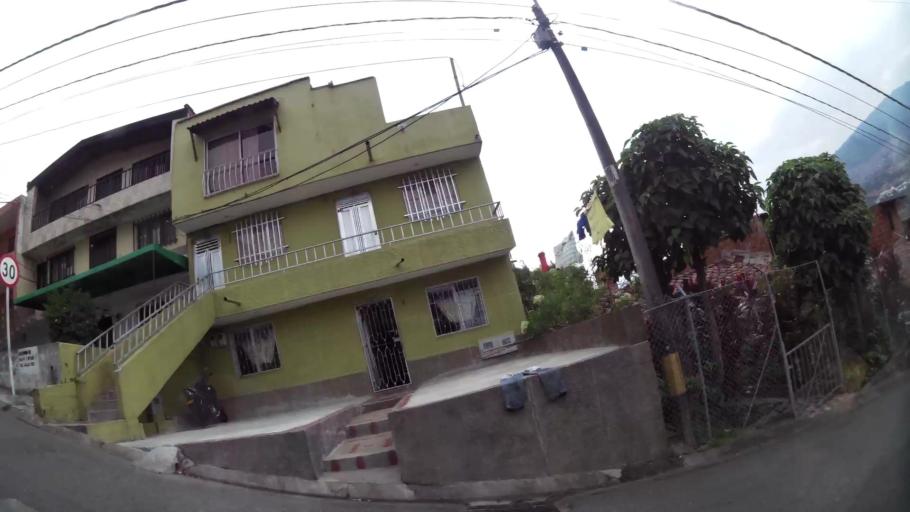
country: CO
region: Antioquia
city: Bello
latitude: 6.3009
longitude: -75.5534
